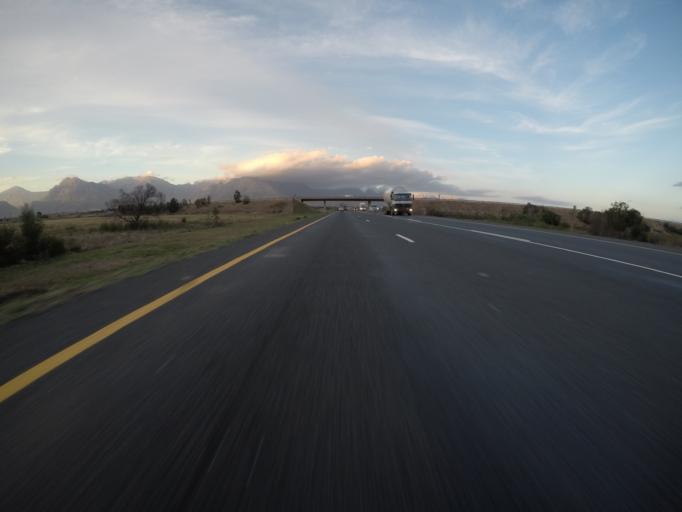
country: ZA
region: Western Cape
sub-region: Cape Winelands District Municipality
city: Worcester
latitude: -33.6485
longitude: 19.3000
